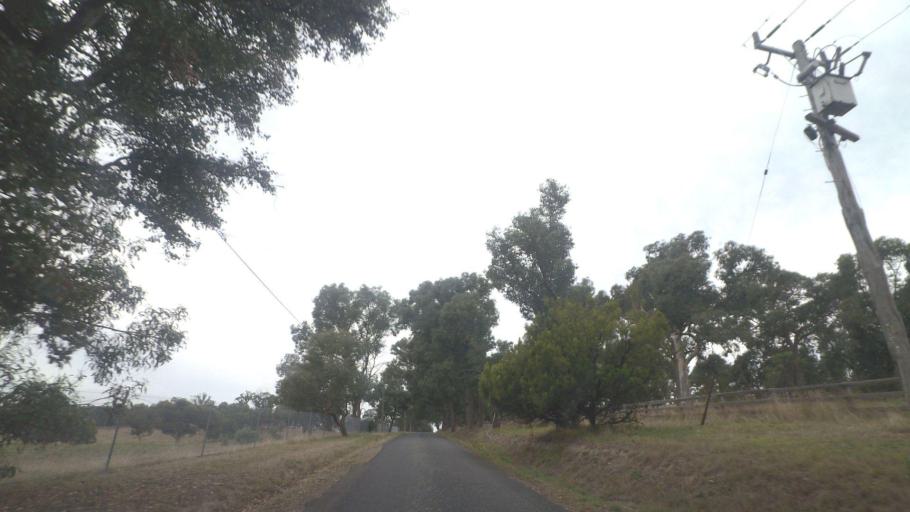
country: AU
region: Victoria
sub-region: Nillumbik
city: North Warrandyte
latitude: -37.7355
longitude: 145.1861
